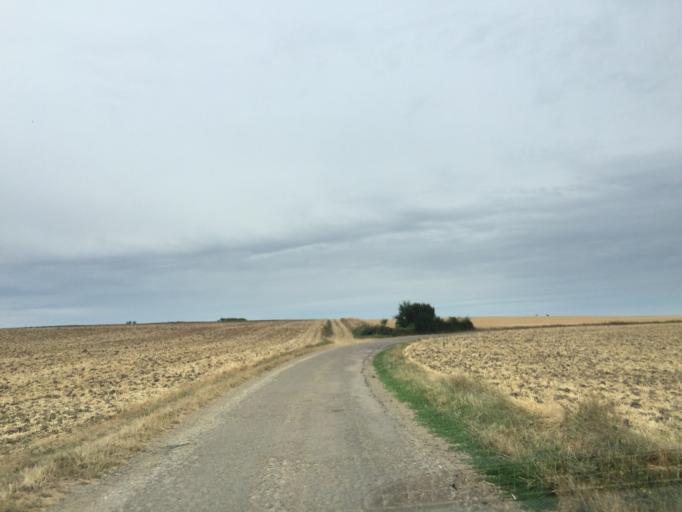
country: FR
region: Bourgogne
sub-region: Departement de l'Yonne
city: Aillant-sur-Tholon
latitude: 47.8639
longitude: 3.3904
